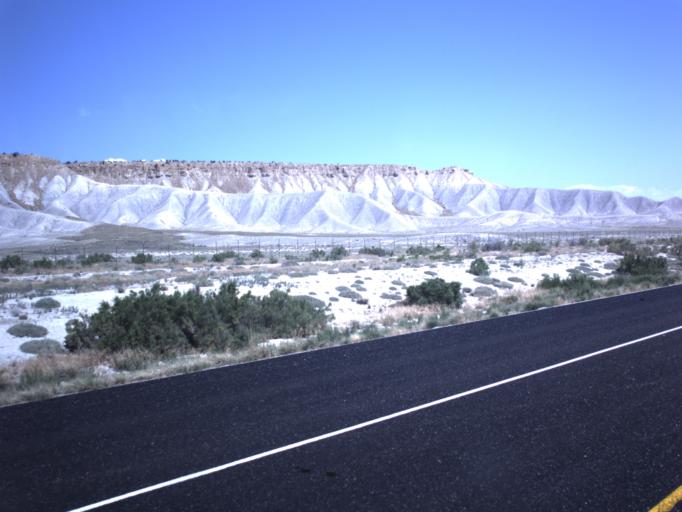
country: US
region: Utah
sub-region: Emery County
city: Ferron
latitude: 39.0207
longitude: -111.1394
